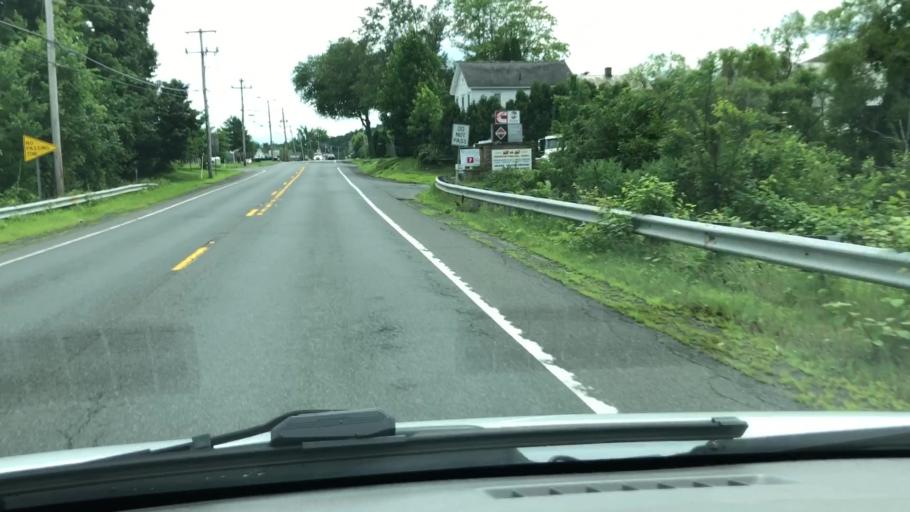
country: US
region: Massachusetts
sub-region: Hampshire County
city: Hatfield
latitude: 42.3717
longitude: -72.6356
